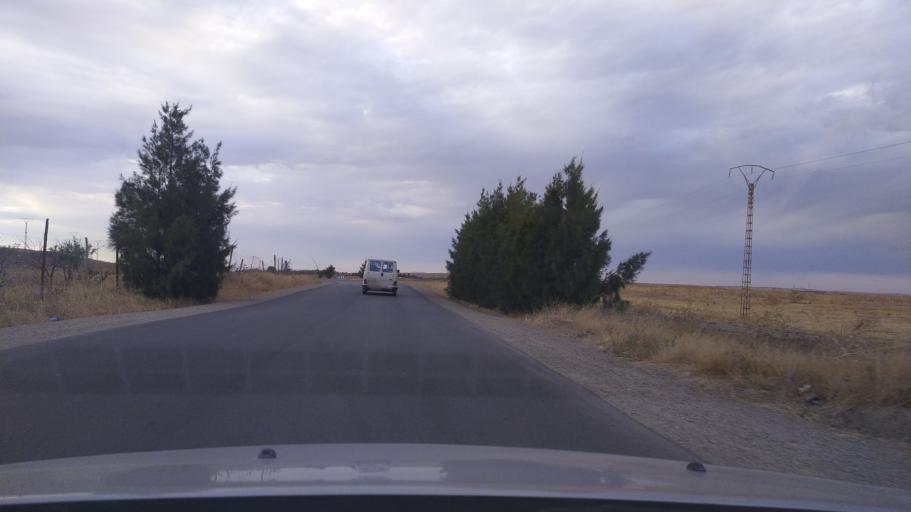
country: DZ
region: Tiaret
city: Frenda
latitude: 35.0130
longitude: 1.1150
